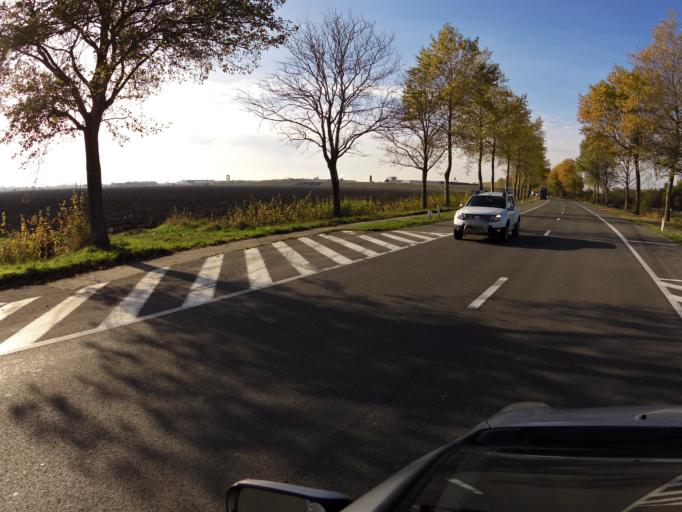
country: BE
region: Flanders
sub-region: Provincie West-Vlaanderen
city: Veurne
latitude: 51.0715
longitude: 2.7065
